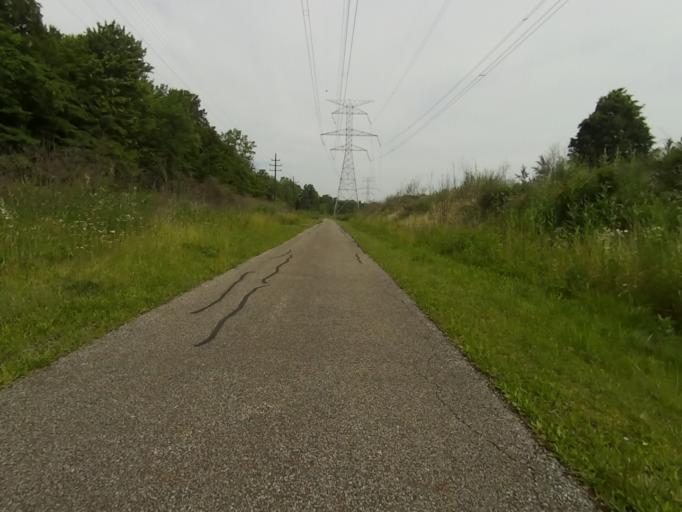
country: US
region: Ohio
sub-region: Summit County
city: Northfield
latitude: 41.3174
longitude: -81.5656
